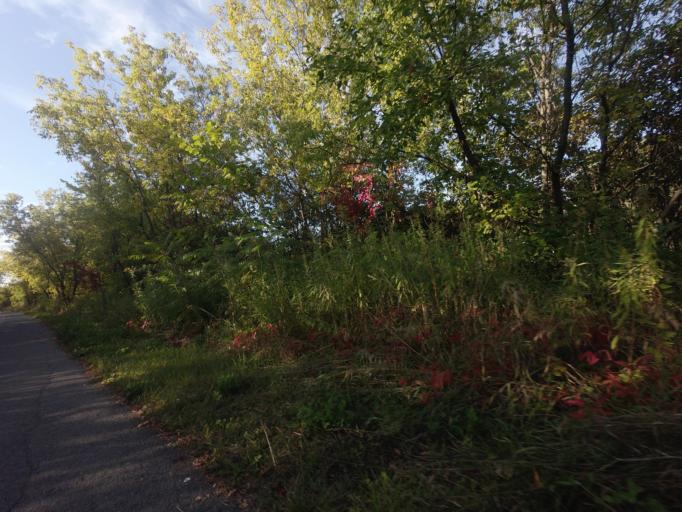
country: CA
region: Quebec
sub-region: Laurentides
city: Saint-Jerome
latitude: 45.8062
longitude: -74.0110
